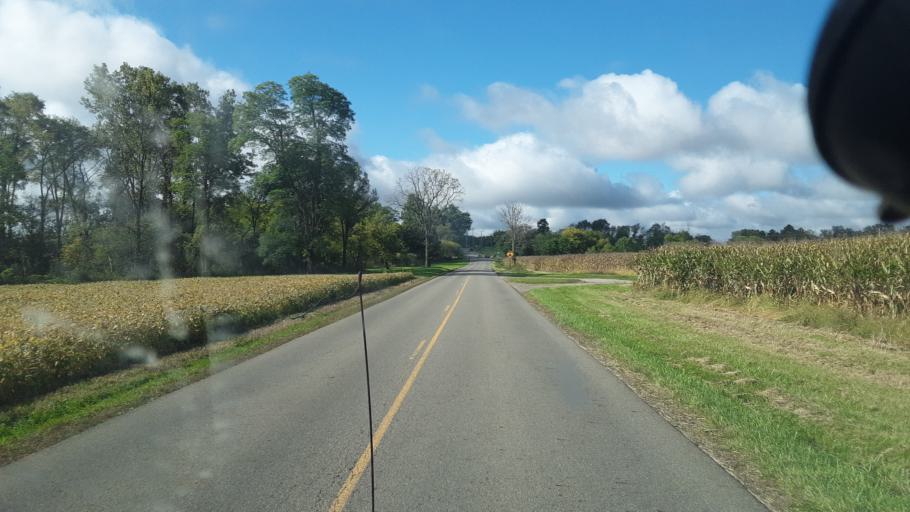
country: US
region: Ohio
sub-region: Knox County
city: Centerburg
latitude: 40.2749
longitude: -82.6536
